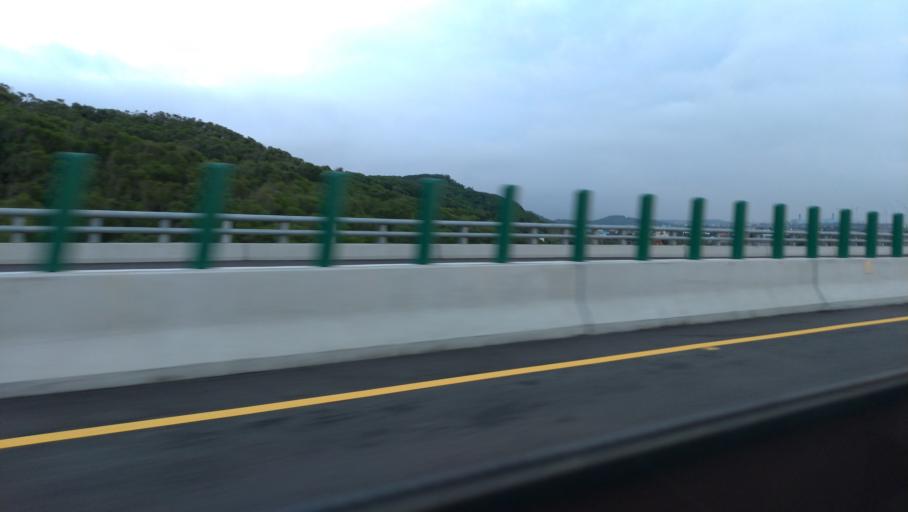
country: TW
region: Taiwan
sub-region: Miaoli
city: Miaoli
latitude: 24.5306
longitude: 120.6943
